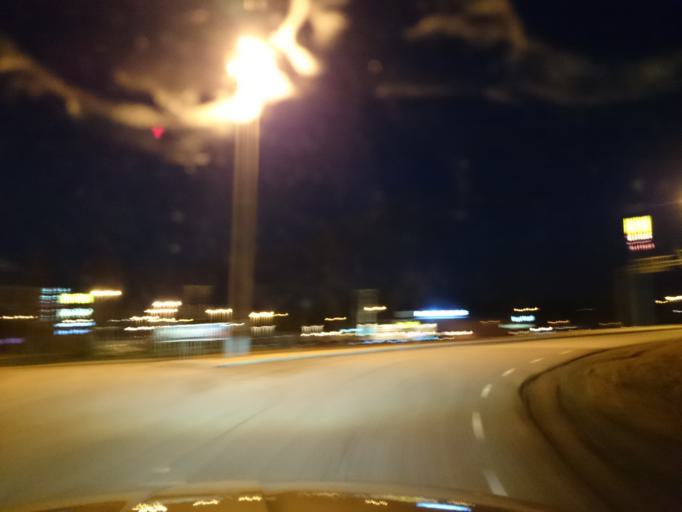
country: SE
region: Stockholm
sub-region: Huddinge Kommun
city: Segeltorp
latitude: 59.2656
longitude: 17.8959
